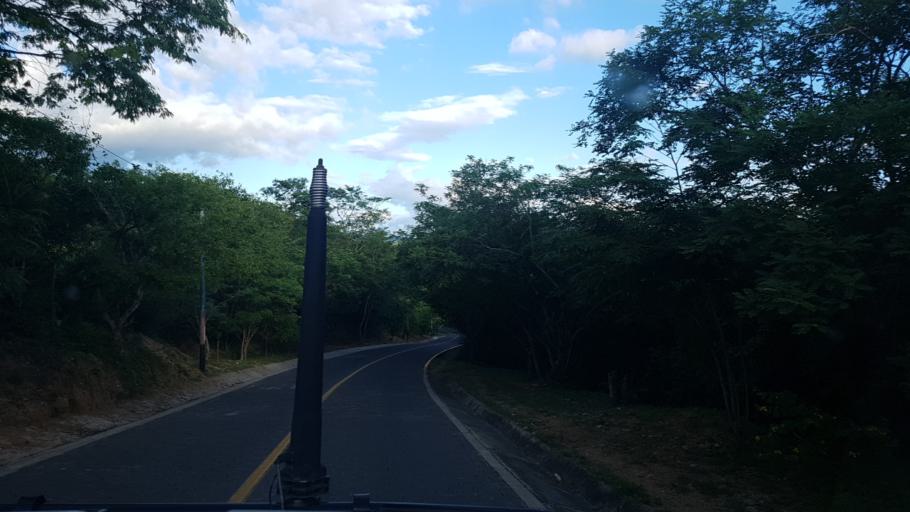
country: NI
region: Nueva Segovia
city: Ocotal
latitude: 13.6435
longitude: -86.5996
